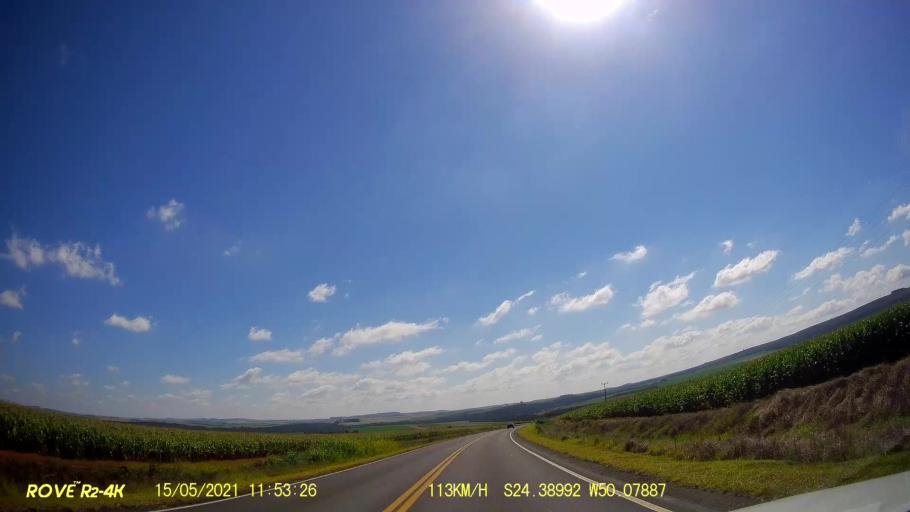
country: BR
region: Parana
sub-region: Pirai Do Sul
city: Pirai do Sul
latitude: -24.3901
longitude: -50.0788
